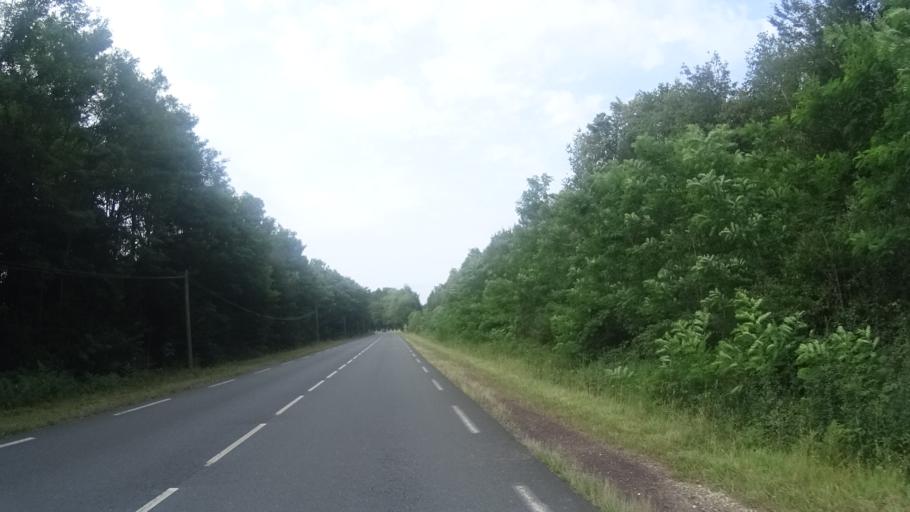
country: FR
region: Aquitaine
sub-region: Departement de la Dordogne
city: Neuvic
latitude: 45.1375
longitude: 0.3954
